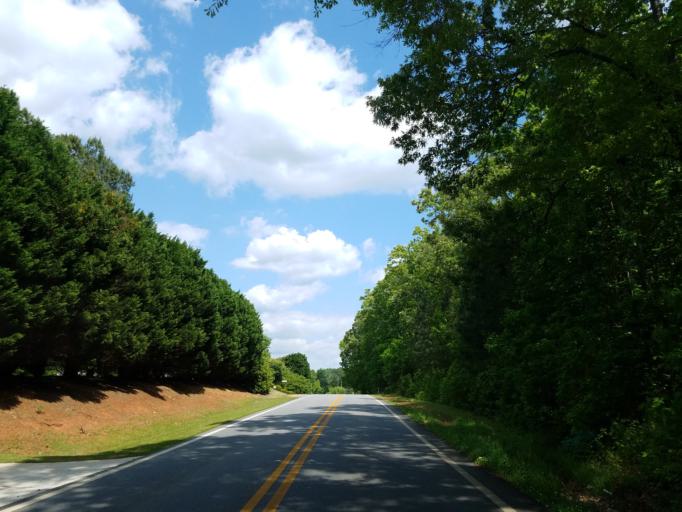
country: US
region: Georgia
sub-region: Bibb County
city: West Point
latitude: 32.9375
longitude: -83.7881
